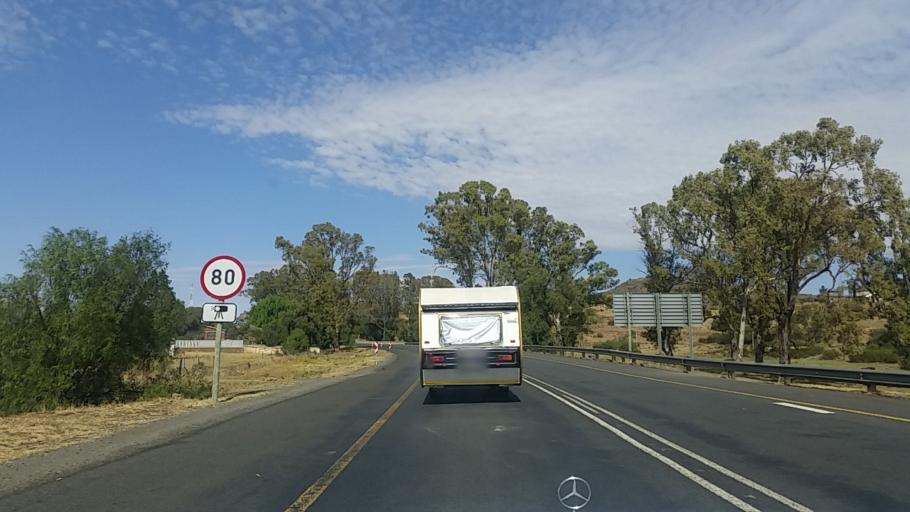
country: ZA
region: Northern Cape
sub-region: Pixley ka Seme District Municipality
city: Colesberg
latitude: -30.7111
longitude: 25.1023
